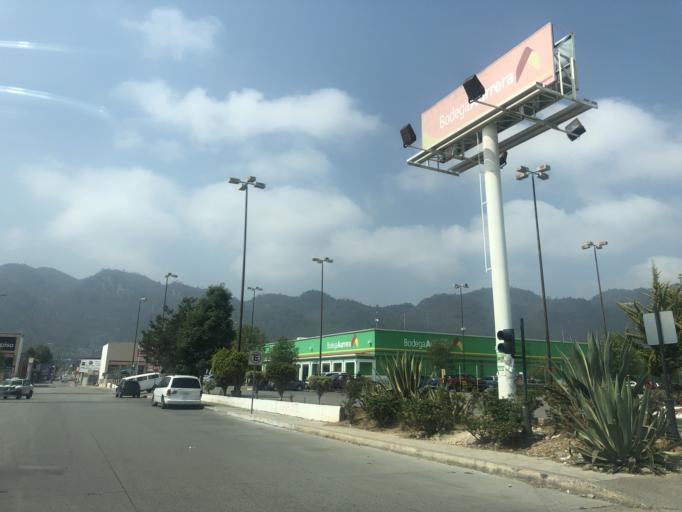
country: MX
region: Chiapas
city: San Cristobal de las Casas
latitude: 16.7214
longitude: -92.6430
